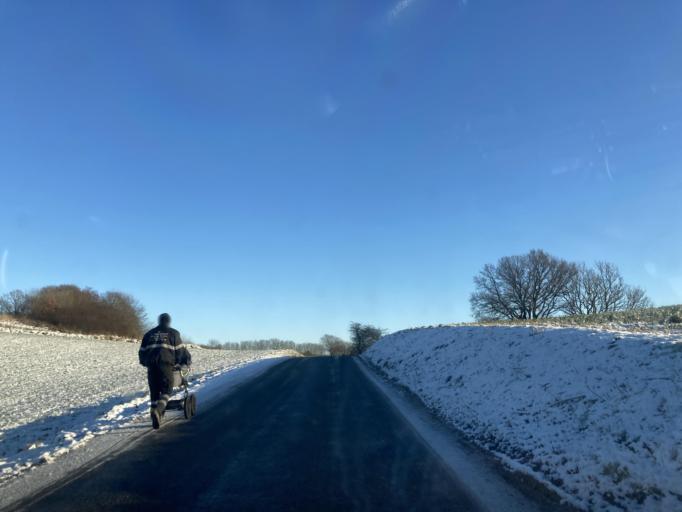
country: DK
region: South Denmark
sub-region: Svendborg Kommune
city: Svendborg
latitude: 55.1263
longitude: 10.5921
